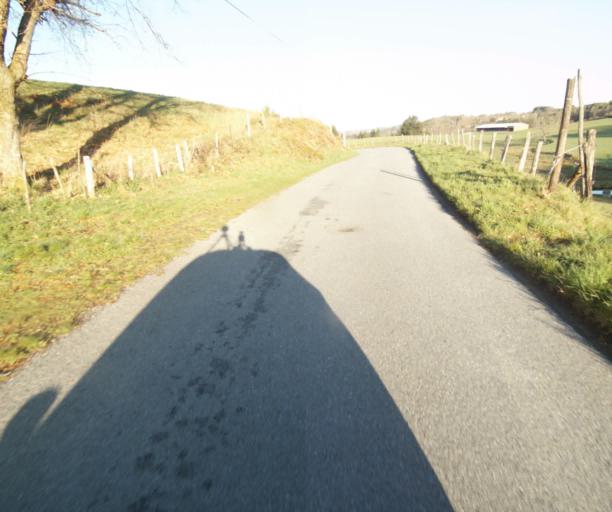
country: FR
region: Limousin
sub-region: Departement de la Correze
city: Correze
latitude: 45.3753
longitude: 1.8601
